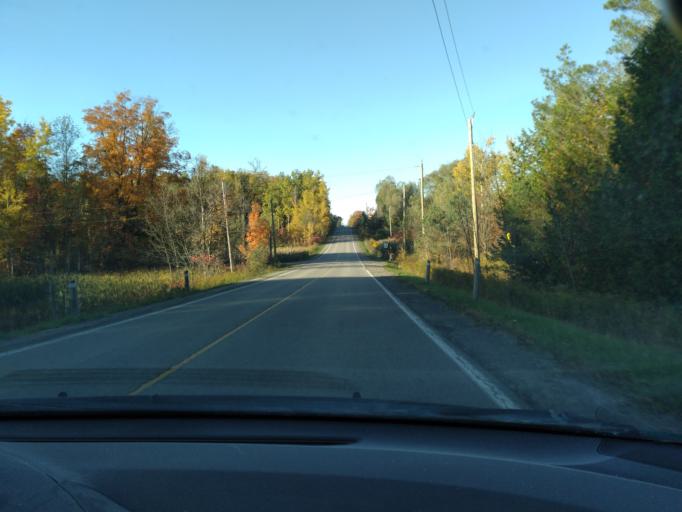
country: CA
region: Ontario
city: Bradford West Gwillimbury
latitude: 43.9696
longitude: -79.7200
